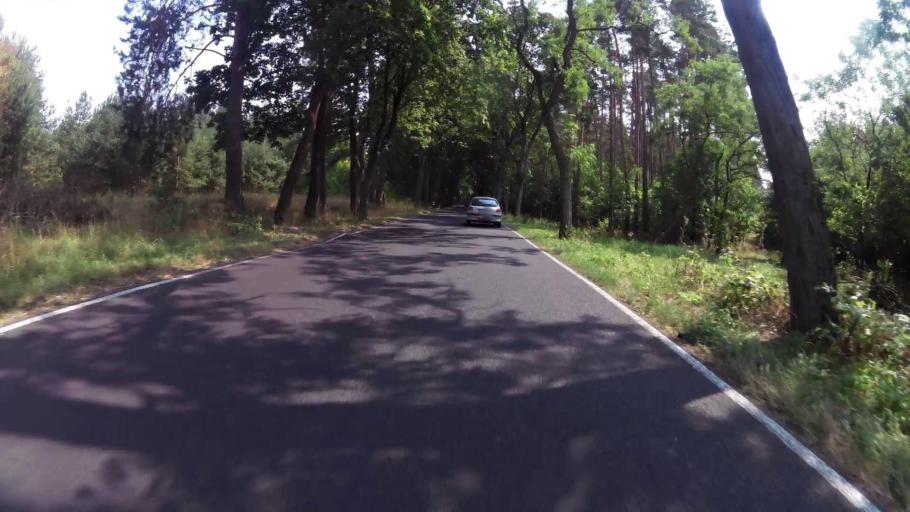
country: PL
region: West Pomeranian Voivodeship
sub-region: Powiat gryfinski
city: Moryn
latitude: 52.8282
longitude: 14.4219
